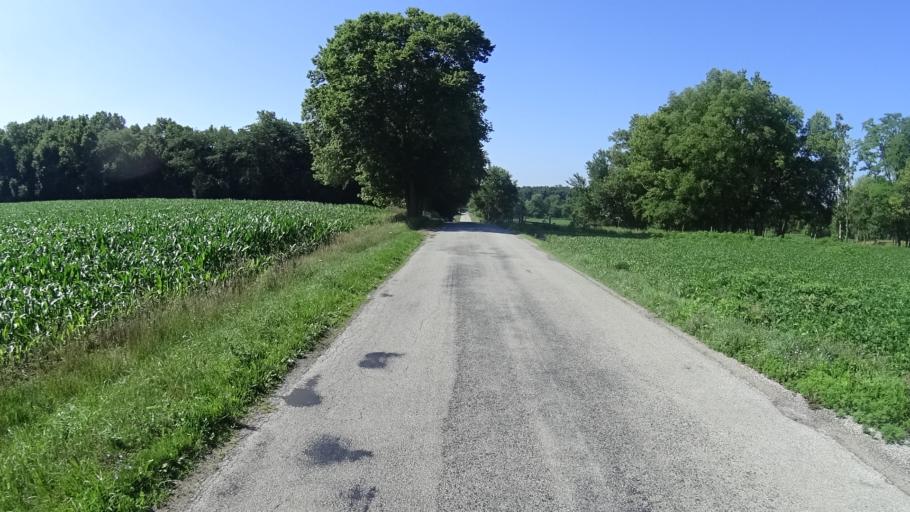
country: US
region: Indiana
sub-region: Madison County
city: Ingalls
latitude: 39.9685
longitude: -85.8151
